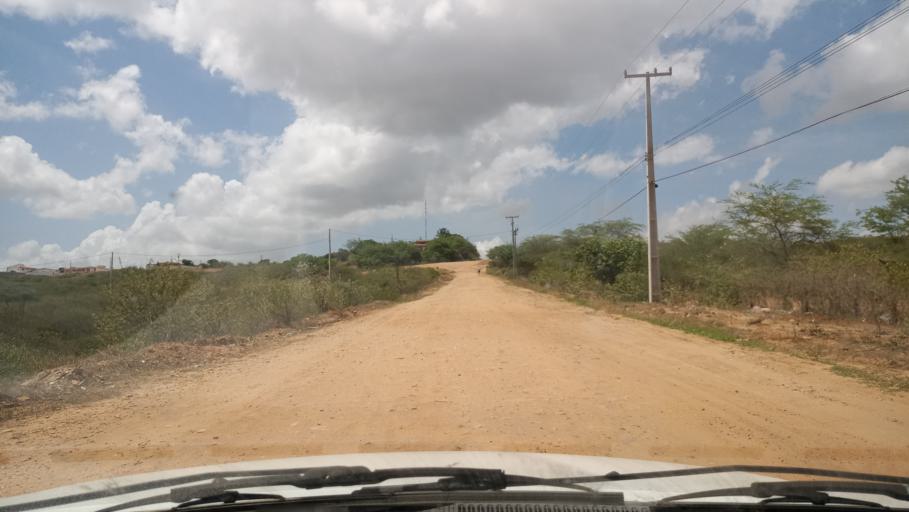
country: BR
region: Rio Grande do Norte
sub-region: Sao Paulo Do Potengi
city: Sao Paulo do Potengi
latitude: -5.9054
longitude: -35.7618
